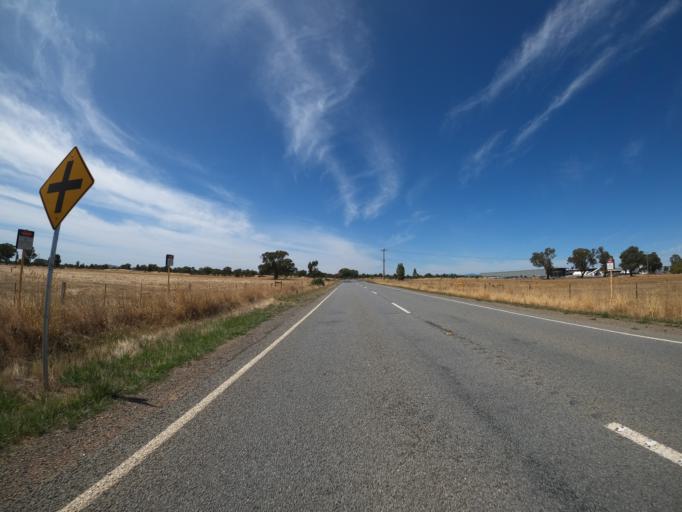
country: AU
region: Victoria
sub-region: Benalla
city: Benalla
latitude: -36.5156
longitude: 146.0318
